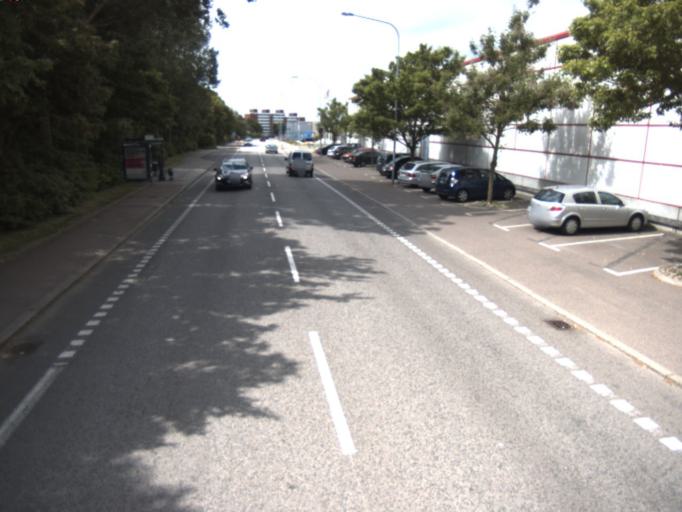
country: SE
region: Skane
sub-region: Helsingborg
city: Helsingborg
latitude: 56.0652
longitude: 12.7207
